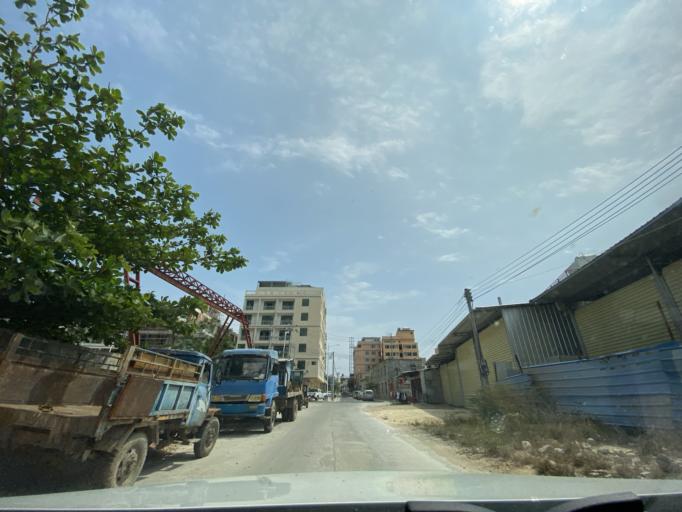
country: CN
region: Hainan
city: Yingzhou
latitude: 18.4256
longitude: 109.8532
